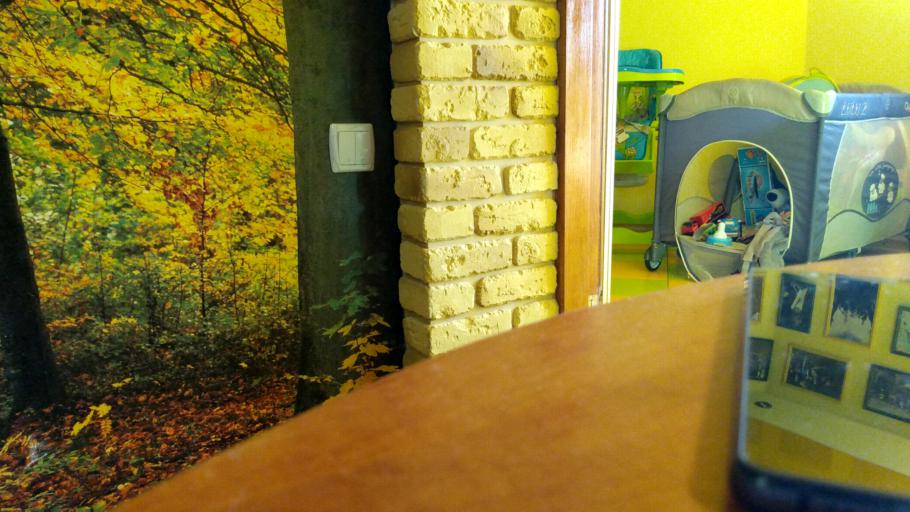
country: RU
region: Tverskaya
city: Likhoslavl'
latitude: 57.2563
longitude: 35.4175
